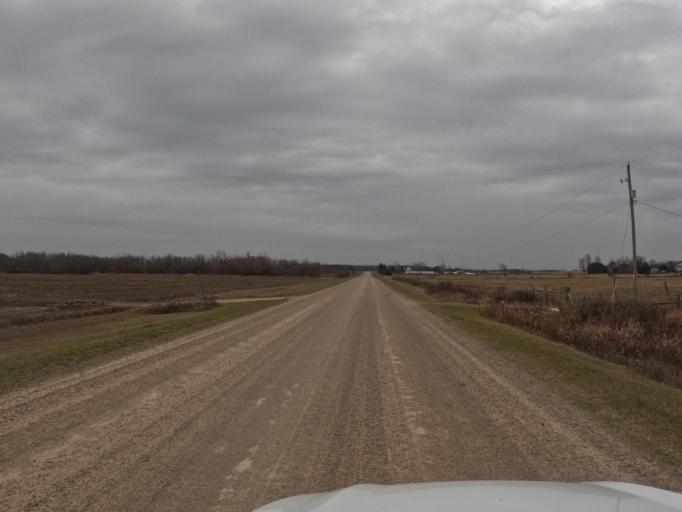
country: CA
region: Ontario
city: Shelburne
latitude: 43.8766
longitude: -80.3570
